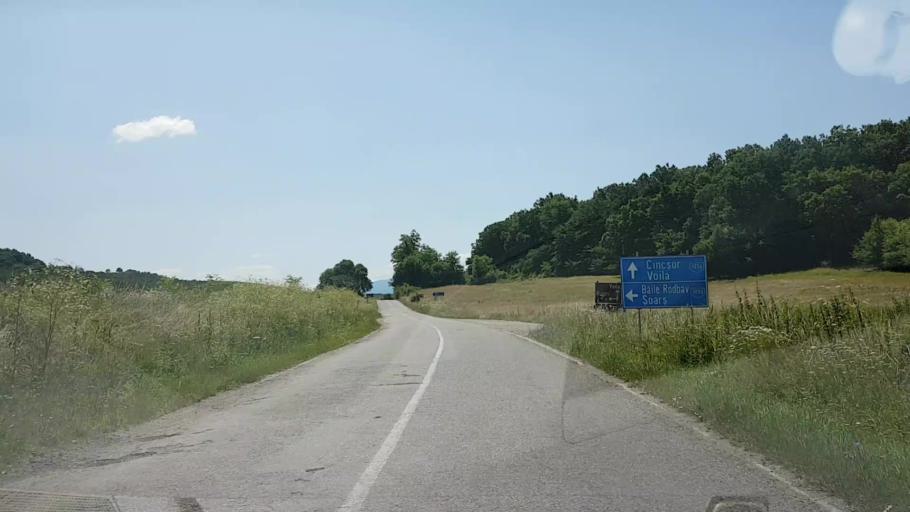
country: RO
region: Brasov
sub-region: Comuna Cincu
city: Cincu
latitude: 45.8711
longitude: 24.8211
